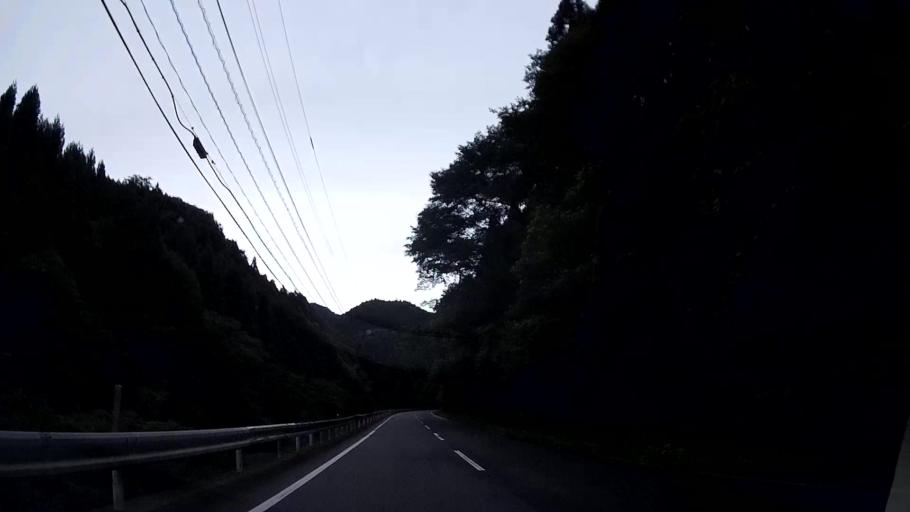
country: JP
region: Kumamoto
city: Kikuchi
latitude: 33.0726
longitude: 130.9191
